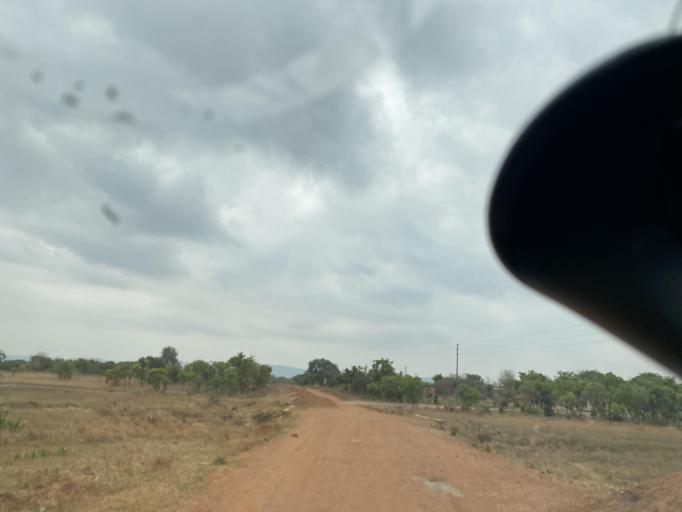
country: ZM
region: Lusaka
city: Chongwe
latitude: -15.2517
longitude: 28.7275
